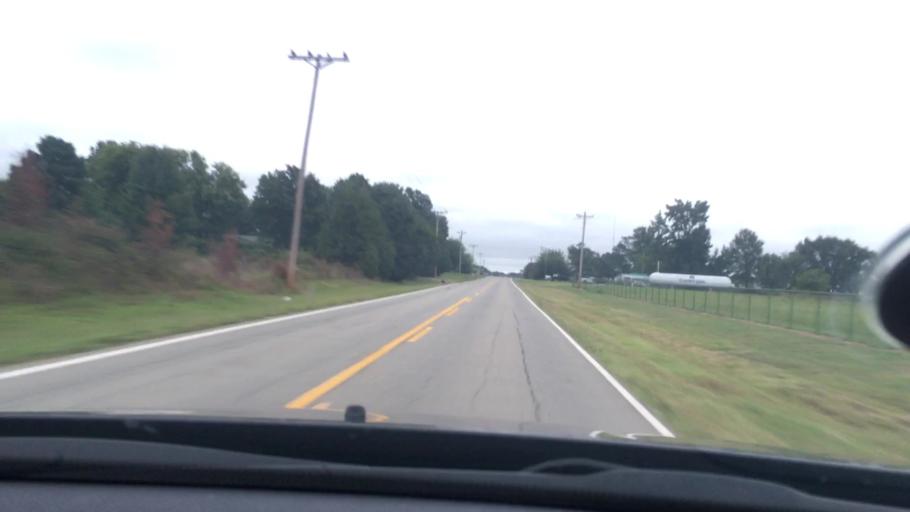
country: US
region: Oklahoma
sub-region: Sequoyah County
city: Vian
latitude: 35.6097
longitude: -94.9937
